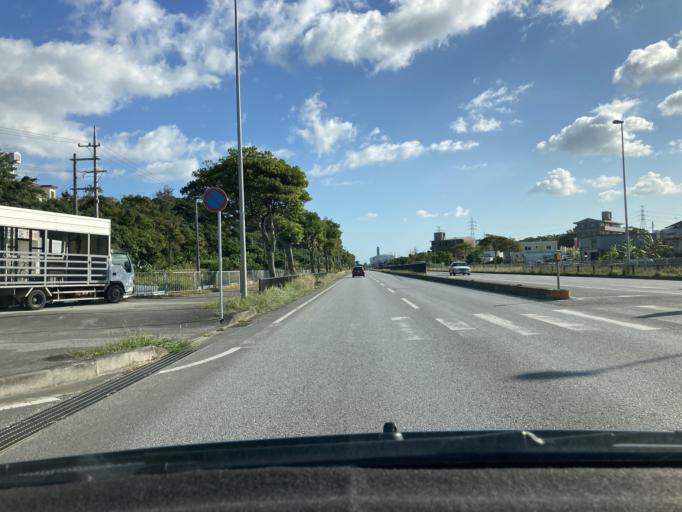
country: JP
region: Okinawa
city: Ishikawa
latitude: 26.4117
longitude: 127.8190
